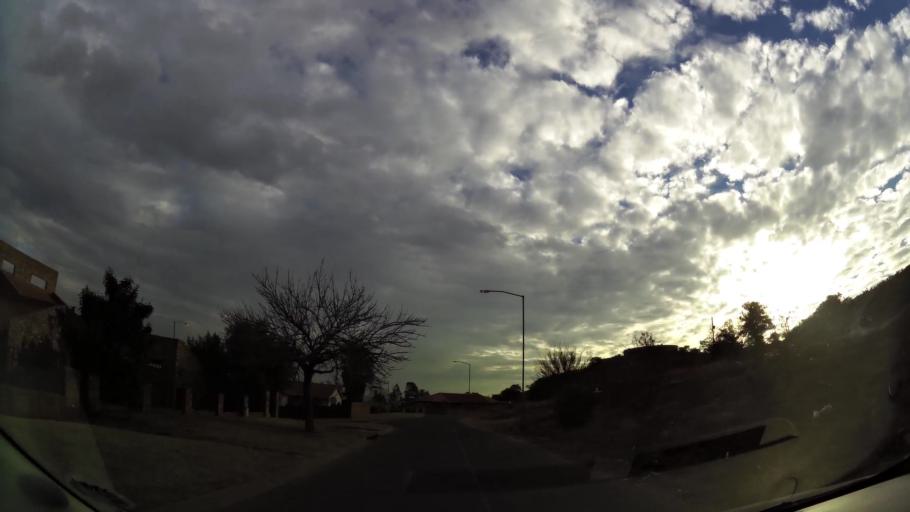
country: ZA
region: Gauteng
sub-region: City of Tshwane Metropolitan Municipality
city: Pretoria
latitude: -25.6986
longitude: 28.3189
